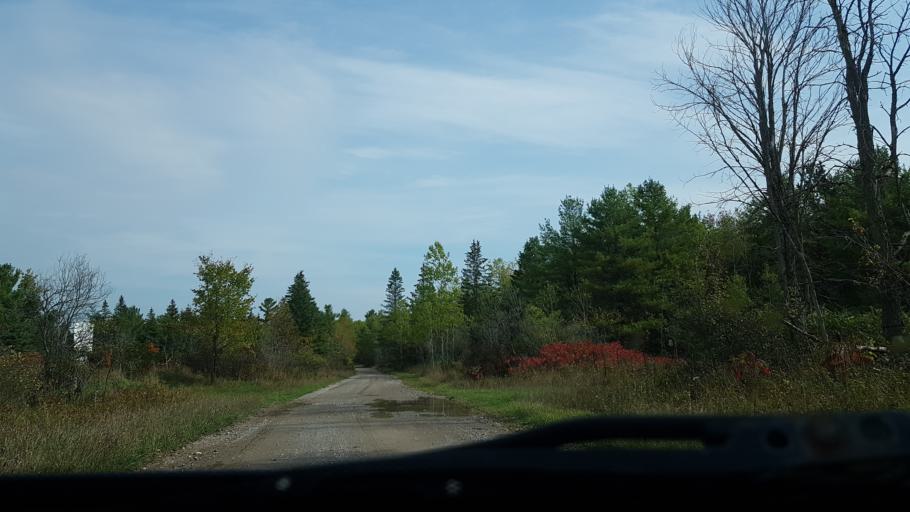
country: CA
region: Ontario
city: Orillia
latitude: 44.6847
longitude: -79.0522
